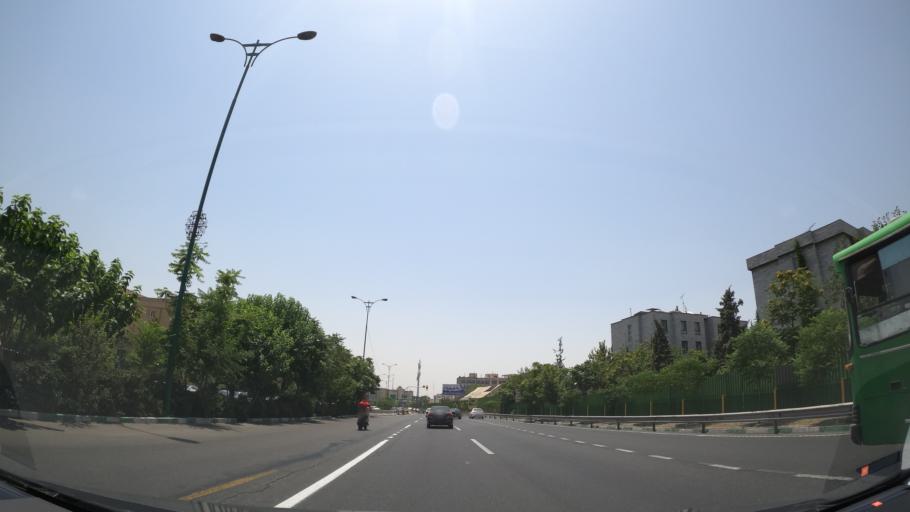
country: IR
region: Tehran
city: Tehran
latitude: 35.7212
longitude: 51.3790
